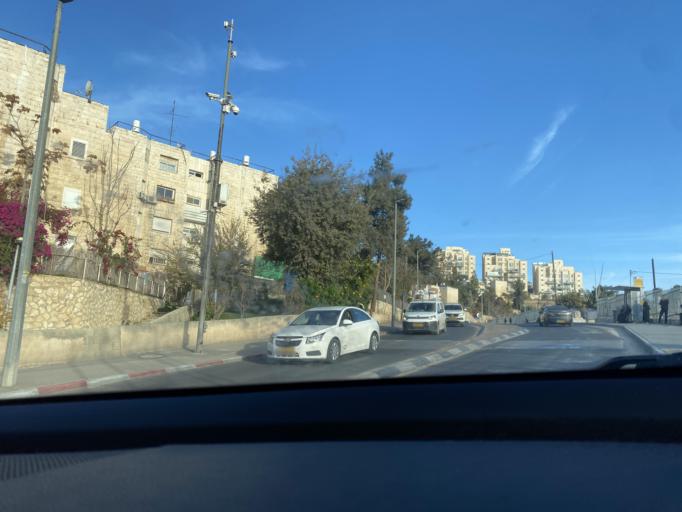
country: PS
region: West Bank
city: Ash Shaykh Sa`d
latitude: 31.7438
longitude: 35.2395
